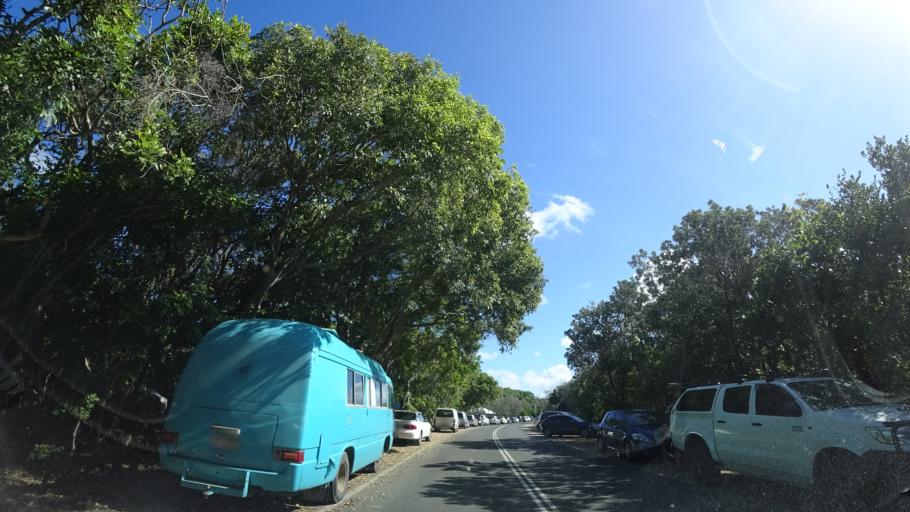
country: AU
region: Queensland
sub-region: Sunshine Coast
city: Mooloolaba
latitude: -26.6381
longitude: 153.1007
